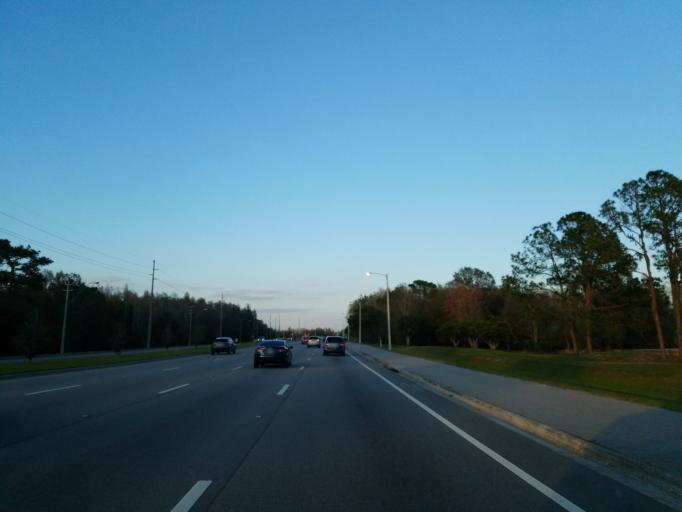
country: US
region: Florida
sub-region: Hillsborough County
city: Pebble Creek
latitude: 28.1389
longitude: -82.3571
